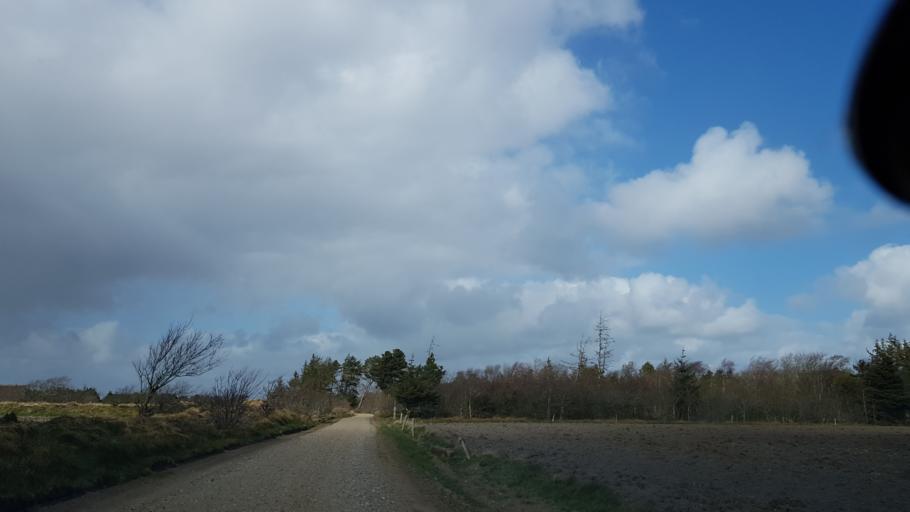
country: DE
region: Schleswig-Holstein
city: List
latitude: 55.1040
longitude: 8.5365
